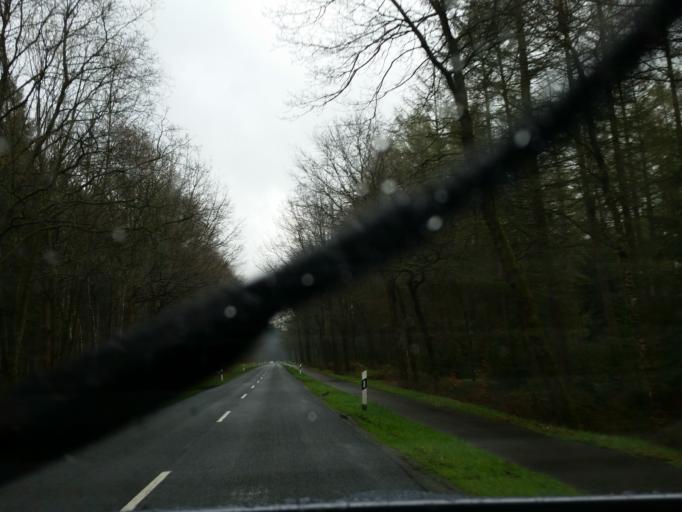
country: DE
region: Lower Saxony
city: Hipstedt
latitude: 53.5019
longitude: 8.9860
